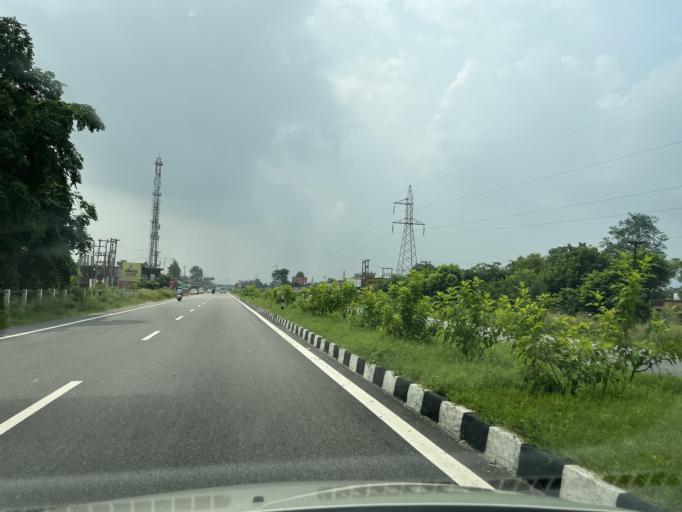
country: IN
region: Uttarakhand
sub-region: Dehradun
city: Raiwala
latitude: 30.0899
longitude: 78.1853
